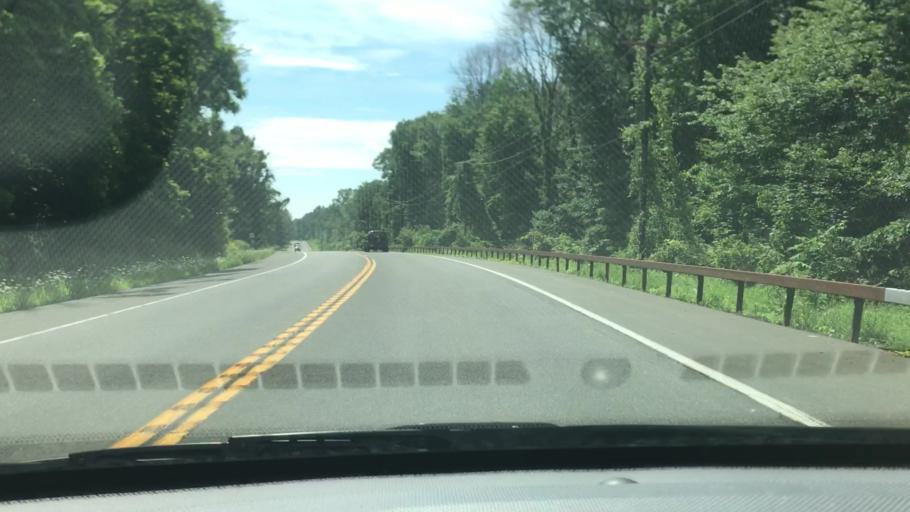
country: US
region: New York
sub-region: Ulster County
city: Shokan
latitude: 41.9834
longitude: -74.2577
